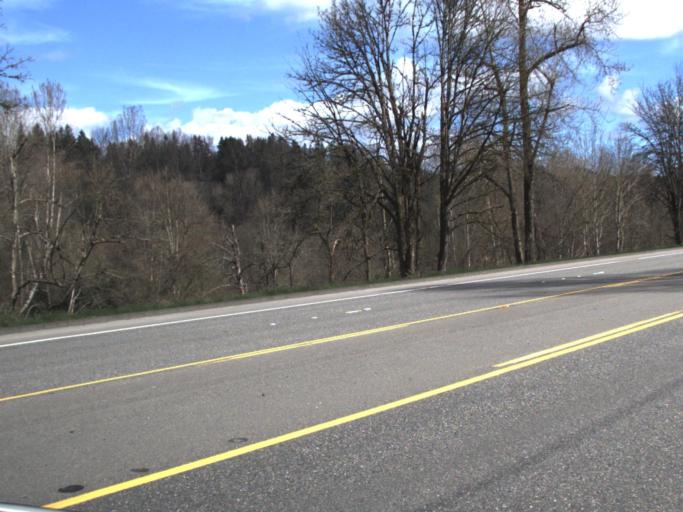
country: US
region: Washington
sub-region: King County
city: East Renton Highlands
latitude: 47.4632
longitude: -122.1198
